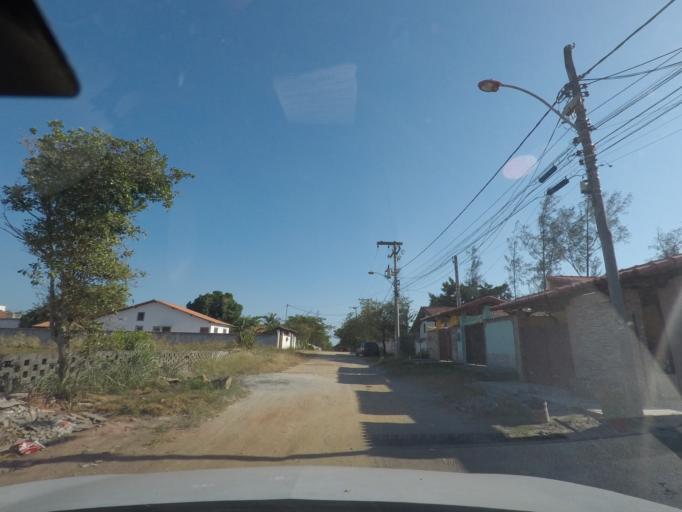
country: BR
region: Rio de Janeiro
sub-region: Marica
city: Marica
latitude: -22.9685
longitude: -42.9262
